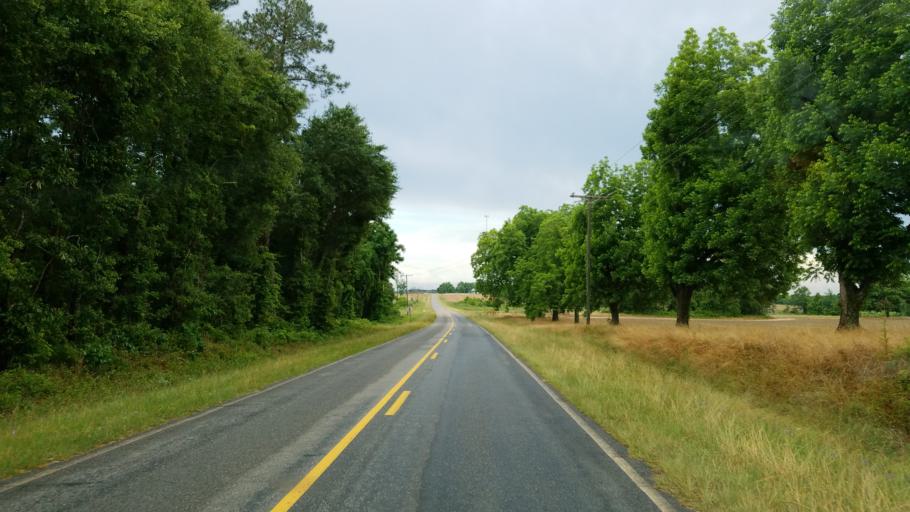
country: US
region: Georgia
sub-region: Dooly County
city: Vienna
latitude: 32.1632
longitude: -83.7988
